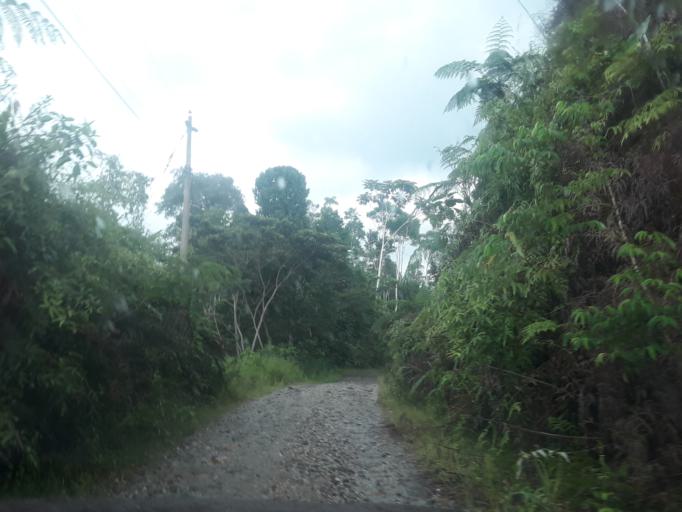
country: EC
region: Napo
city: Tena
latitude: -1.0986
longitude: -77.6953
